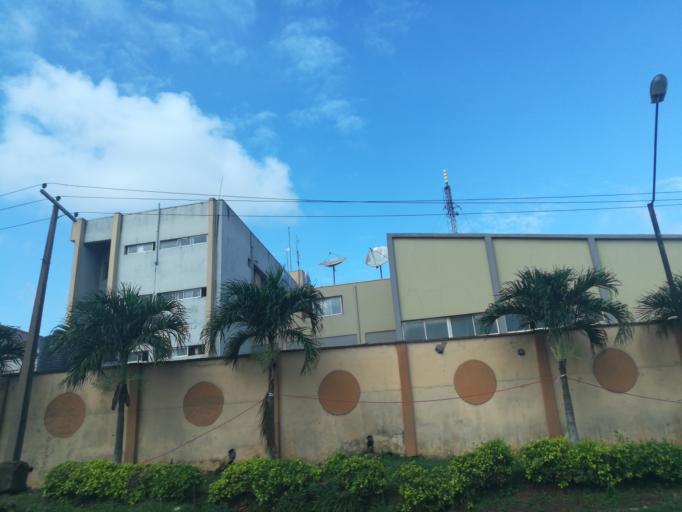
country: NG
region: Lagos
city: Ikeja
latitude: 6.6165
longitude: 3.3536
